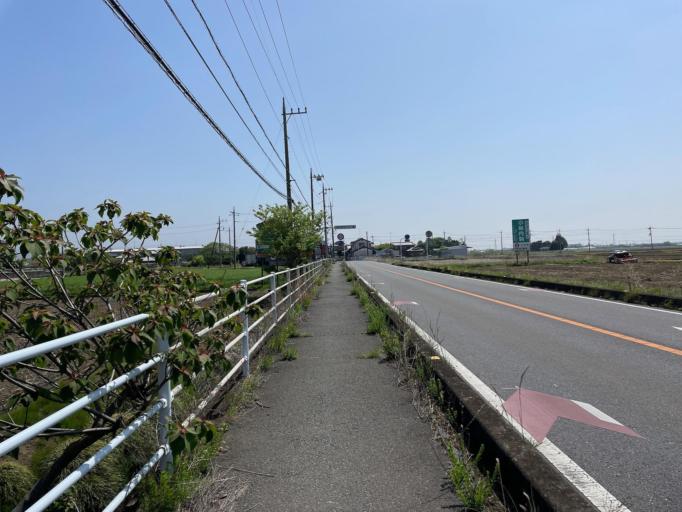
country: JP
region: Tochigi
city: Ashikaga
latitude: 36.3024
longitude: 139.4164
